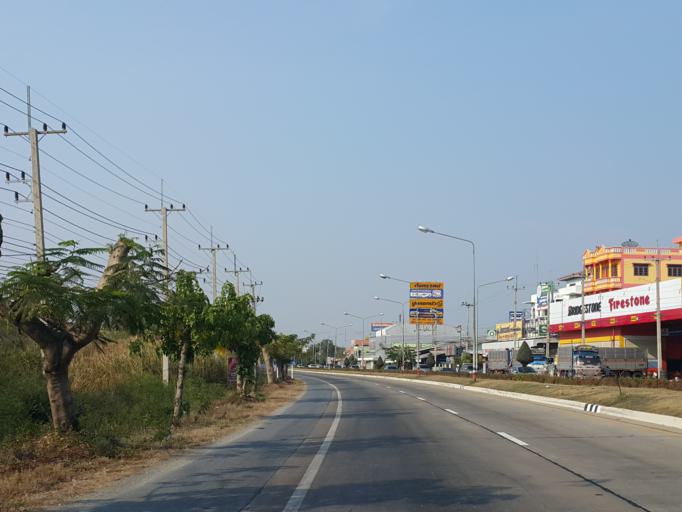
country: TH
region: Suphan Buri
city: Doembang Nangbuat
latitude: 14.8042
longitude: 100.1138
